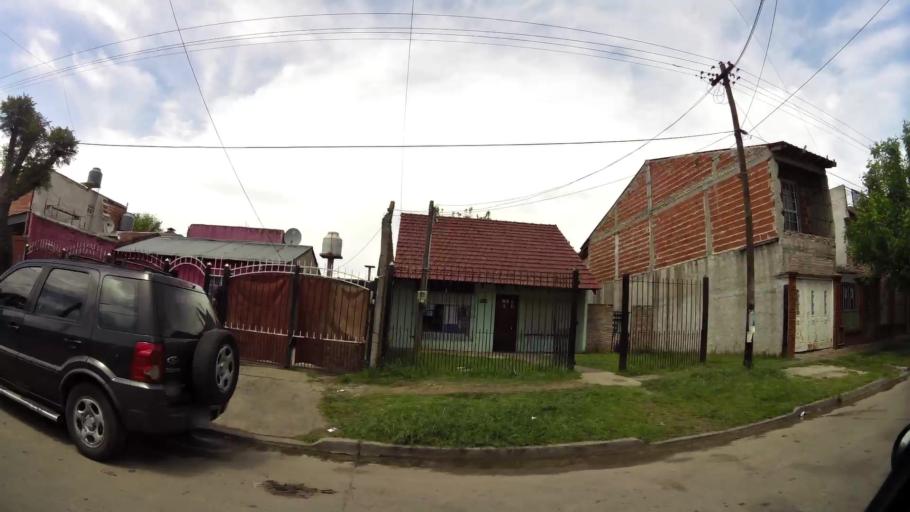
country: AR
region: Buenos Aires
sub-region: Partido de Quilmes
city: Quilmes
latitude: -34.7866
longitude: -58.2603
